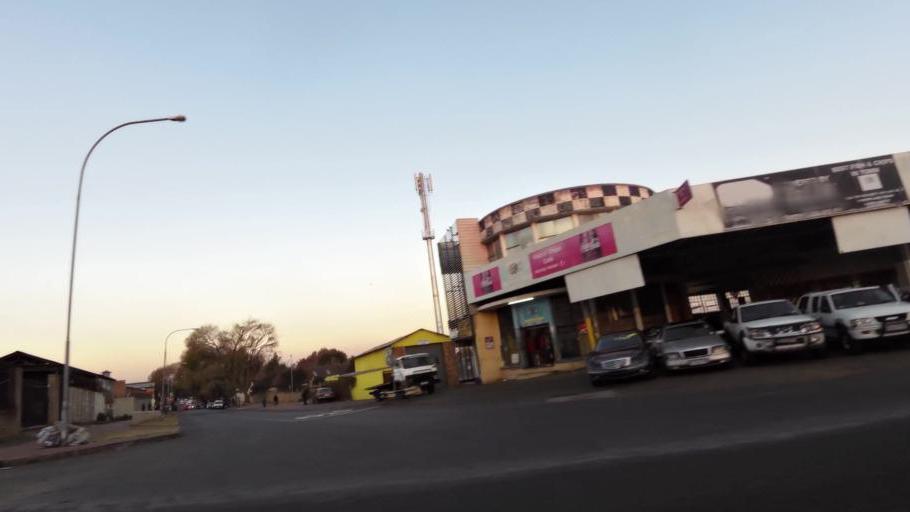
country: ZA
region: Gauteng
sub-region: City of Johannesburg Metropolitan Municipality
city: Johannesburg
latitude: -26.2025
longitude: 27.9883
